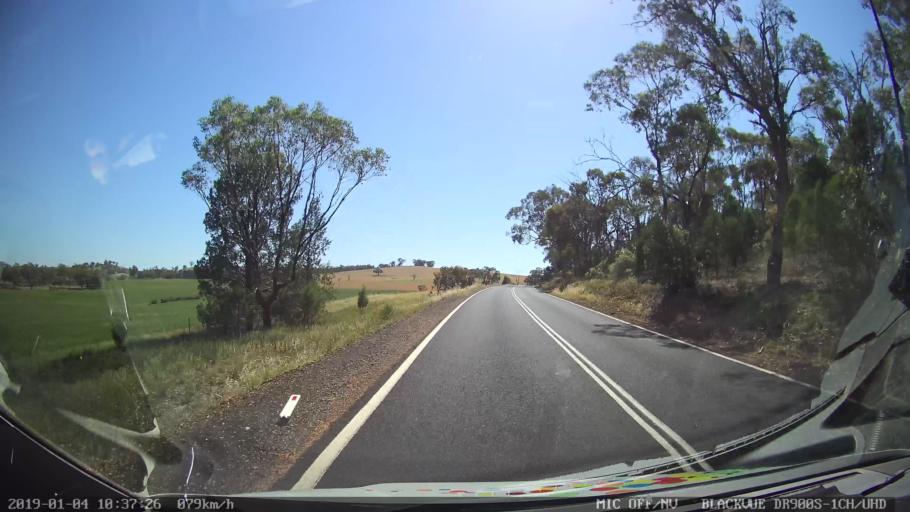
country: AU
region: New South Wales
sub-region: Cabonne
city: Canowindra
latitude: -33.2960
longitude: 148.6946
